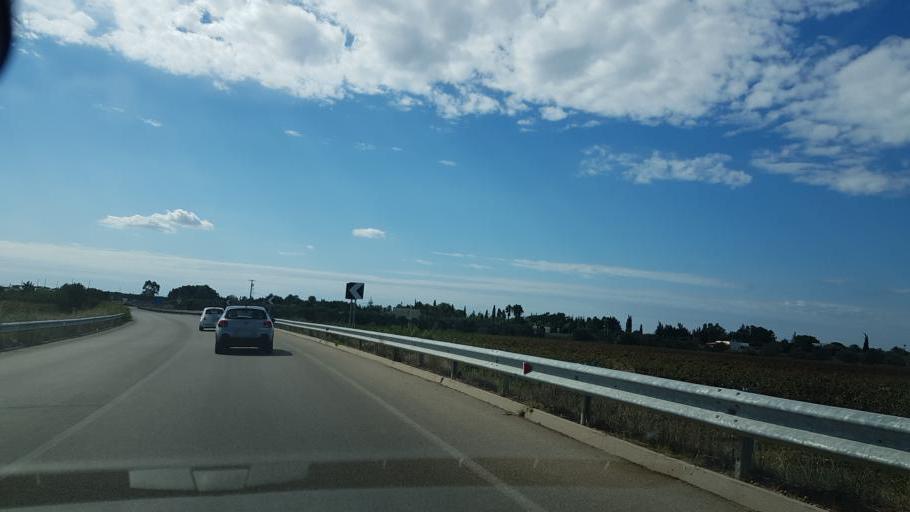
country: IT
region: Apulia
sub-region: Provincia di Lecce
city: Leverano
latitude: 40.2897
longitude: 17.9693
